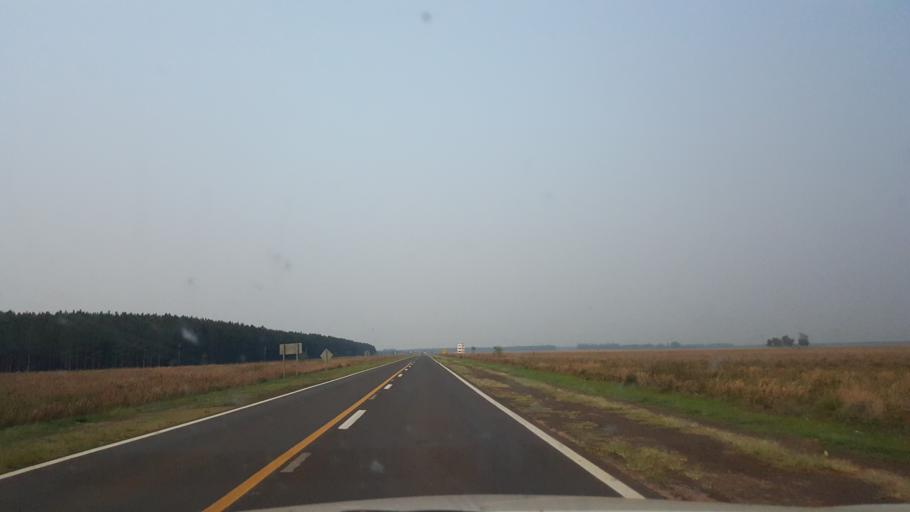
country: AR
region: Corrientes
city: Ituzaingo
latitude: -27.6331
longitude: -56.8995
